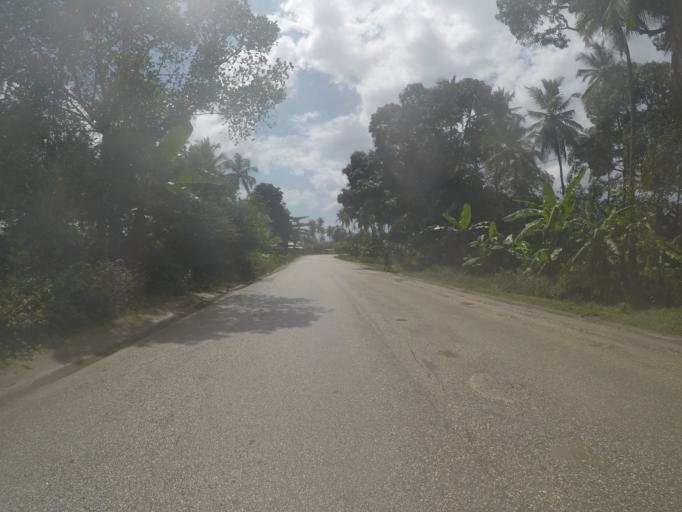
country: TZ
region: Zanzibar North
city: Gamba
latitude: -5.9821
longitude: 39.2504
